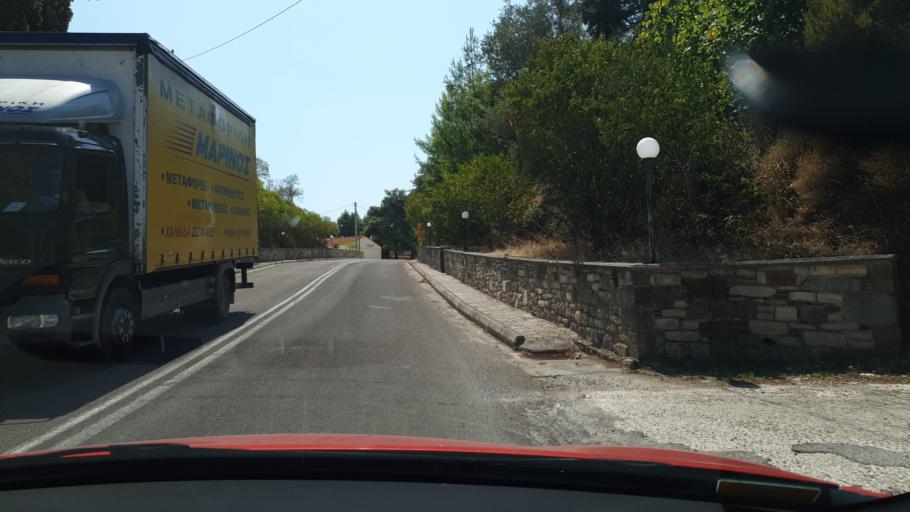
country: GR
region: Central Greece
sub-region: Nomos Evvoias
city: Oxilithos
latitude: 38.5702
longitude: 24.0614
